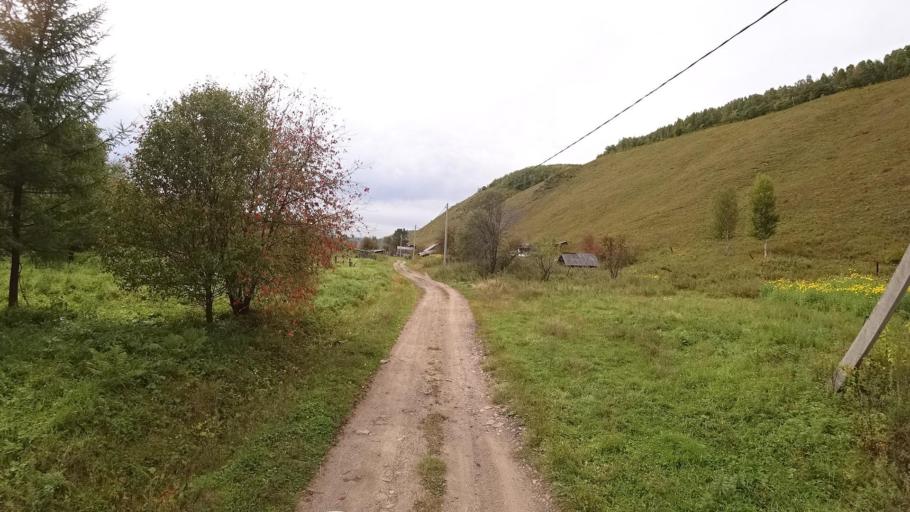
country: RU
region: Jewish Autonomous Oblast
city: Khingansk
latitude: 49.1291
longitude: 131.1844
